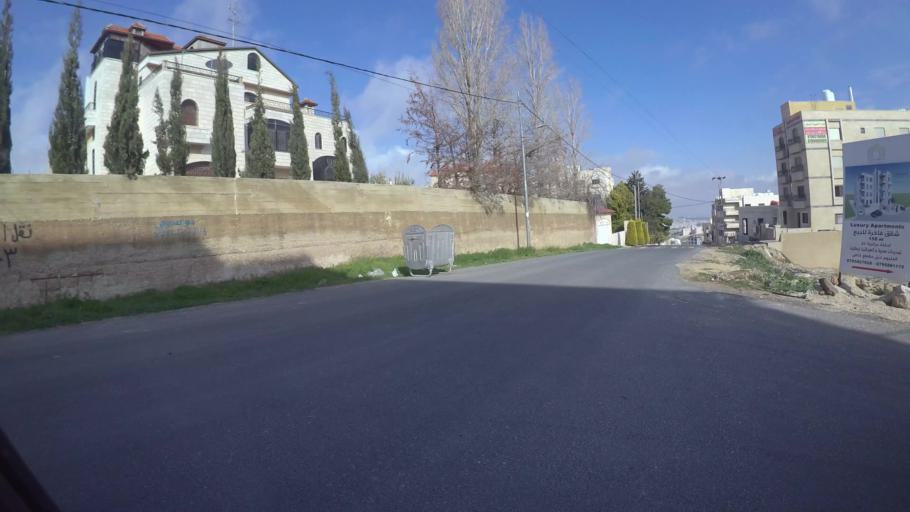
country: JO
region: Amman
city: Al Jubayhah
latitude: 32.0406
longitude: 35.8717
